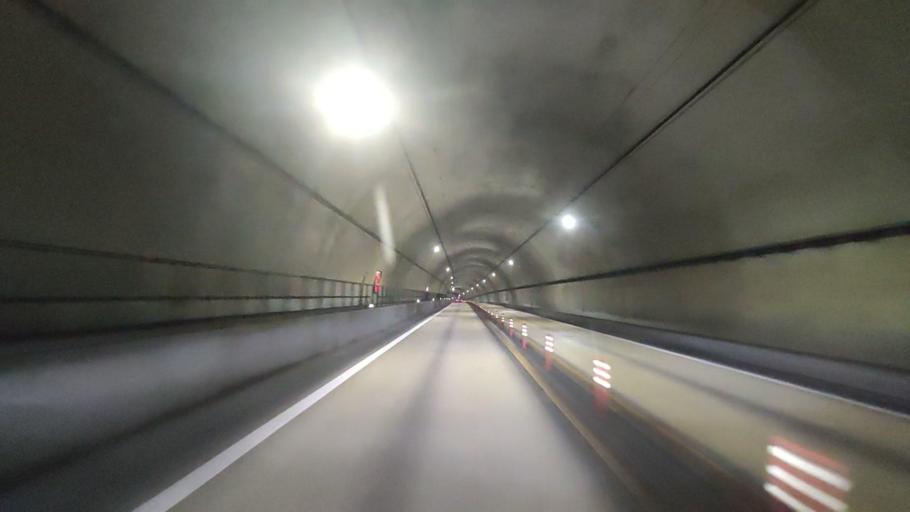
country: JP
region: Wakayama
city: Tanabe
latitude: 33.5709
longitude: 135.4824
